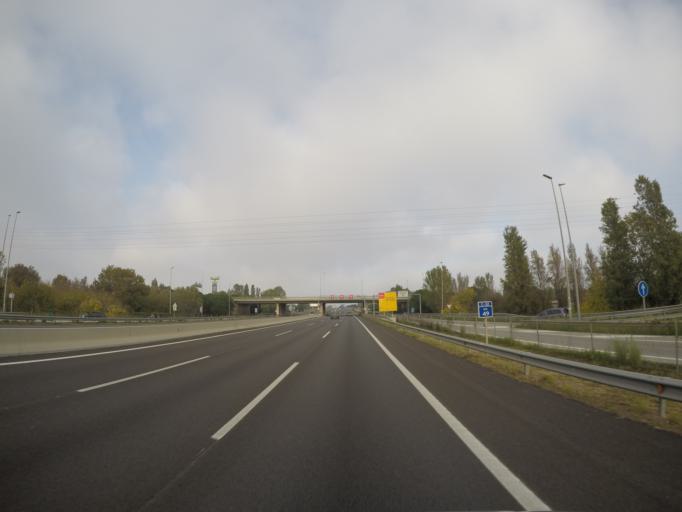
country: ES
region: Catalonia
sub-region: Provincia de Barcelona
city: Gava
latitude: 41.2916
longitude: 2.0085
